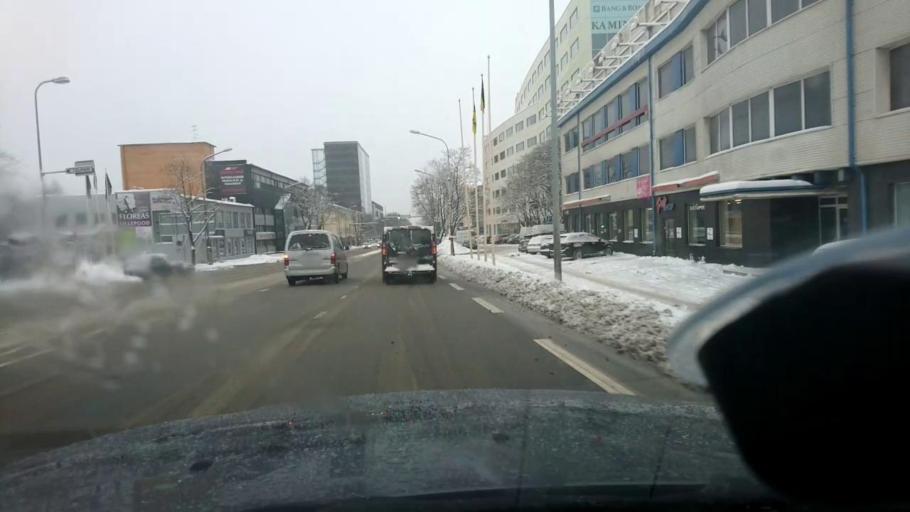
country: EE
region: Harju
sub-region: Tallinna linn
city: Tallinn
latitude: 59.4040
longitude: 24.7308
